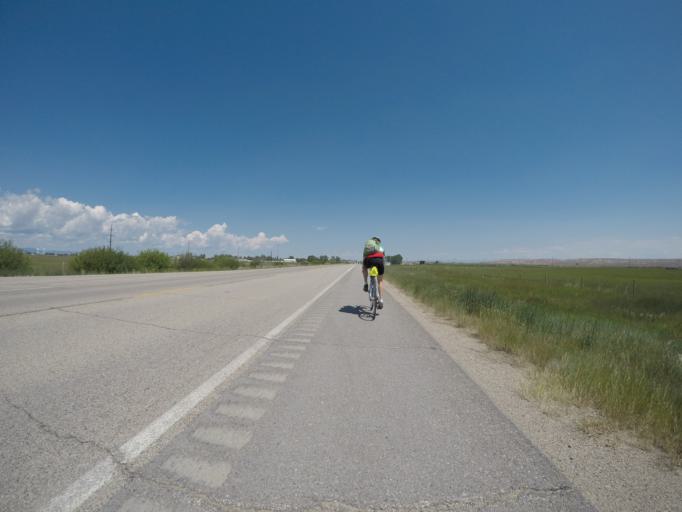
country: US
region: Wyoming
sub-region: Sublette County
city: Marbleton
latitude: 42.5305
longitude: -110.1098
